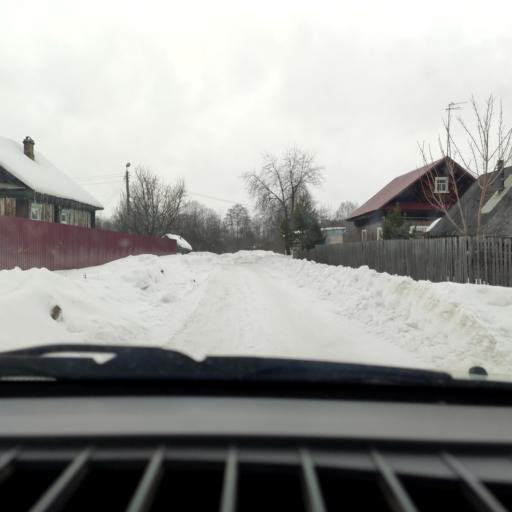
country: RU
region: Perm
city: Krasnokamsk
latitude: 58.0986
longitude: 55.8048
